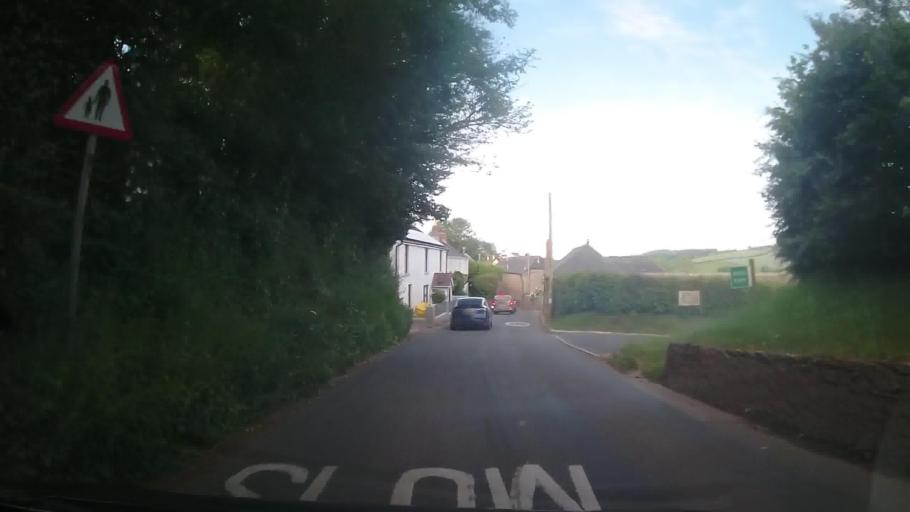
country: GB
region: England
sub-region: Devon
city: Kingsbridge
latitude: 50.2706
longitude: -3.7396
